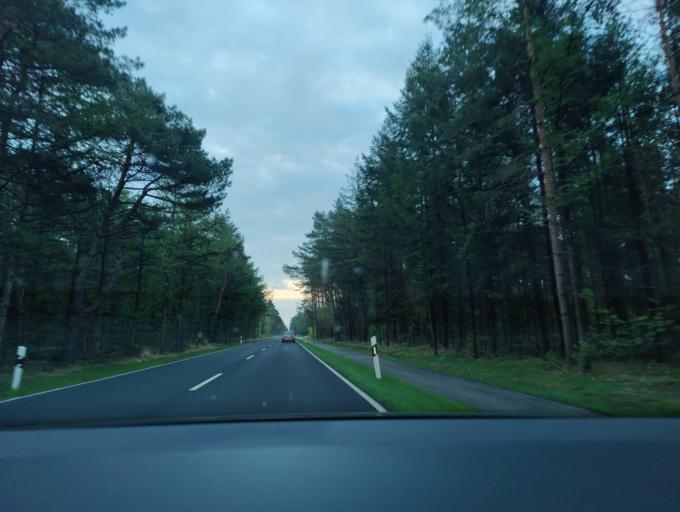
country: DE
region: Lower Saxony
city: Emsburen
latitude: 52.4613
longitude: 7.2718
